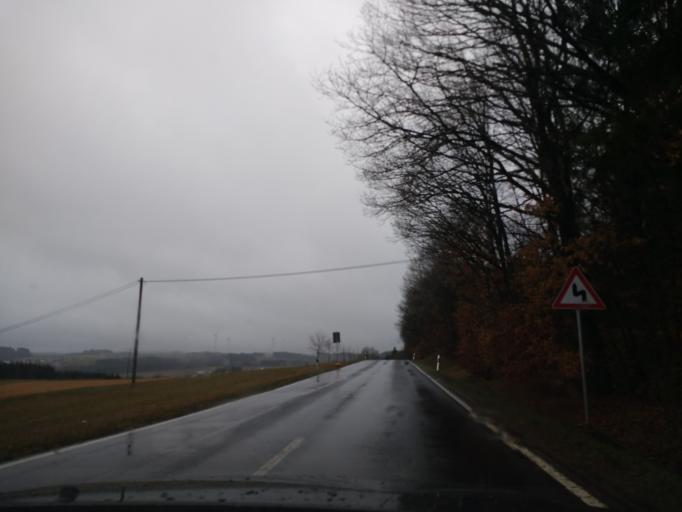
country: DE
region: Rheinland-Pfalz
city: Hinzert-Polert
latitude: 49.7164
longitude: 6.9027
